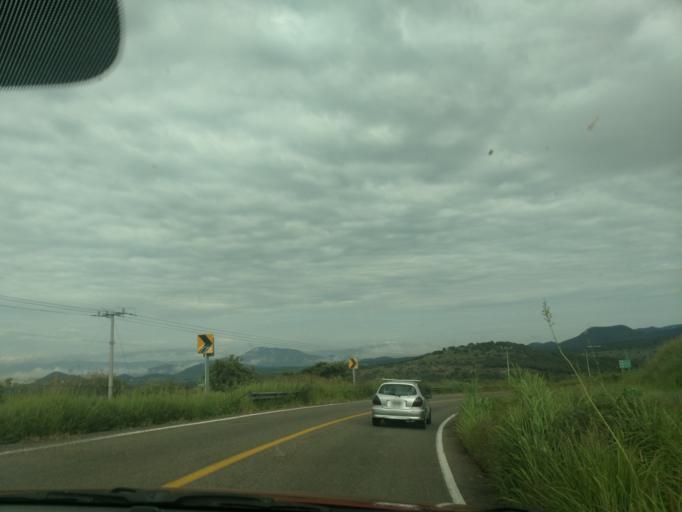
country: MX
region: Jalisco
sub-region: Atengo
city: Soyatlan del Oro
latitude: 20.5437
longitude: -104.2961
